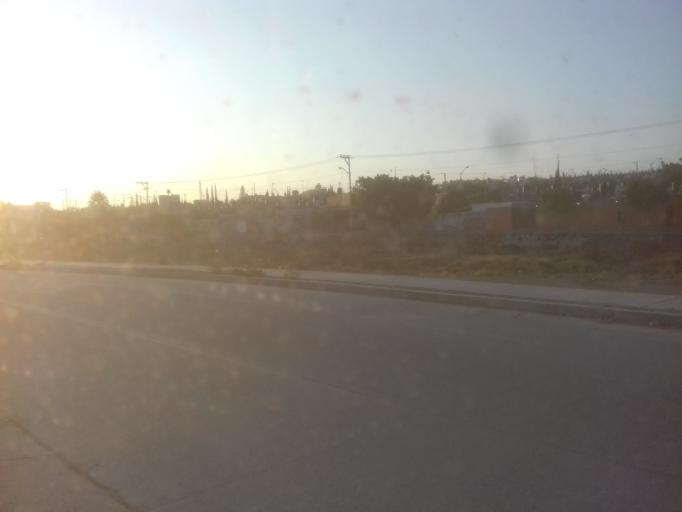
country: MX
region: Aguascalientes
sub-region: Aguascalientes
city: San Sebastian [Fraccionamiento]
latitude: 21.8500
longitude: -102.2600
